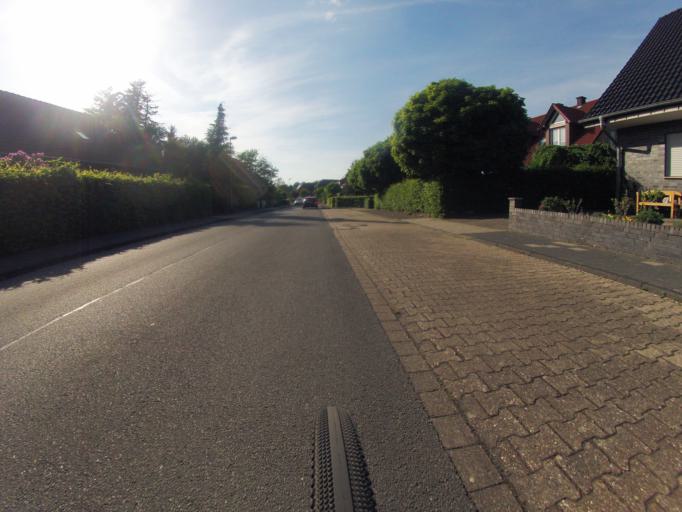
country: DE
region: North Rhine-Westphalia
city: Ibbenburen
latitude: 52.2900
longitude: 7.7120
